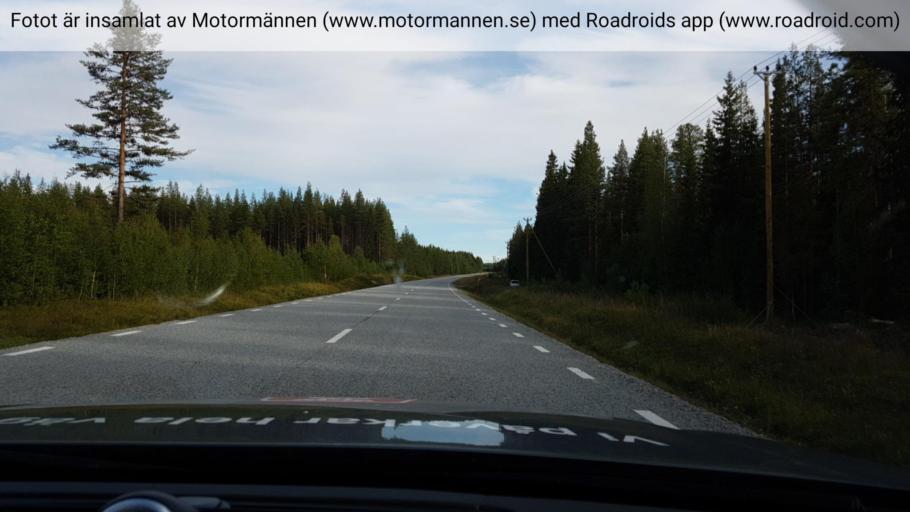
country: SE
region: Jaemtland
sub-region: Stroemsunds Kommun
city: Stroemsund
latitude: 64.2076
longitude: 15.5881
